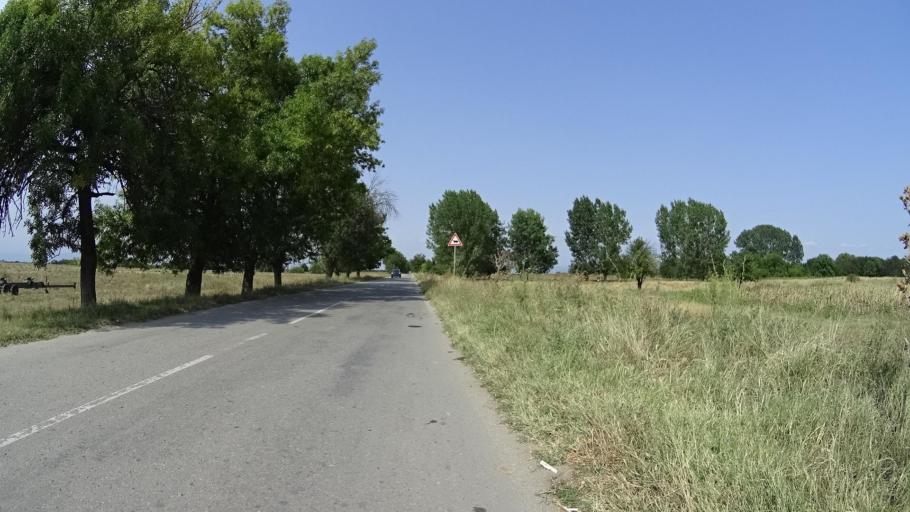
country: BG
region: Plovdiv
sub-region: Obshtina Plovdiv
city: Plovdiv
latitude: 42.2476
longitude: 24.7963
